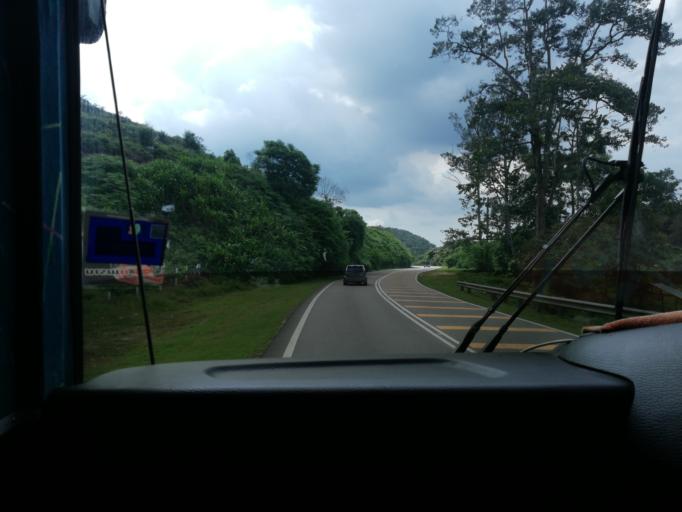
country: MY
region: Kedah
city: Kulim
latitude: 5.3093
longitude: 100.6091
